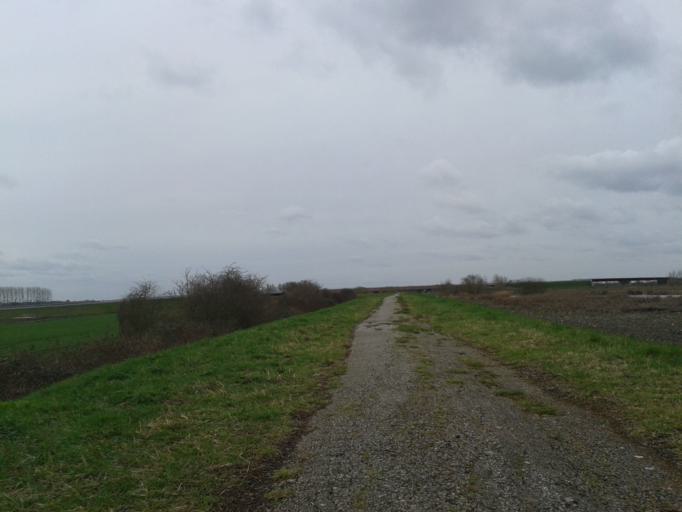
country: GB
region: England
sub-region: Cambridgeshire
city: Ely
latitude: 52.3879
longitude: 0.2692
